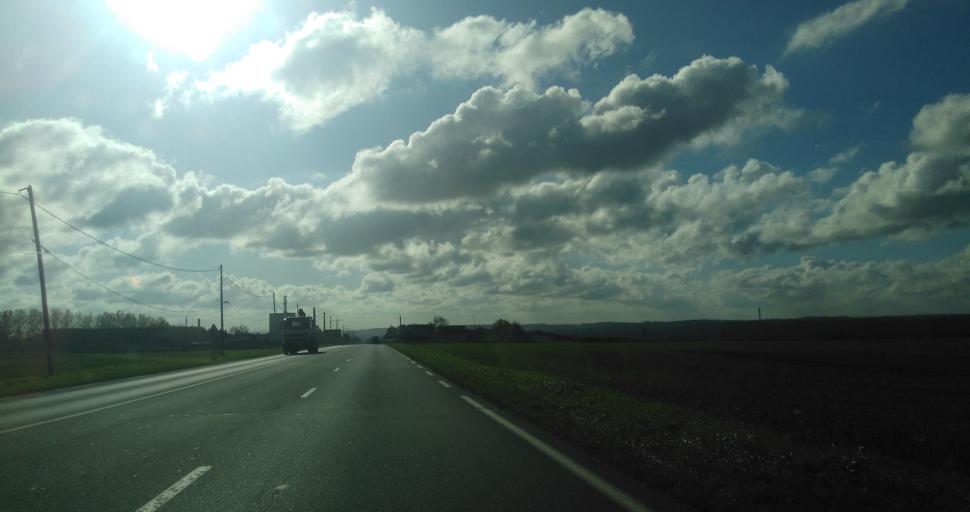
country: FR
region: Picardie
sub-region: Departement de la Somme
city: Abbeville
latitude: 50.1296
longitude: 1.8277
